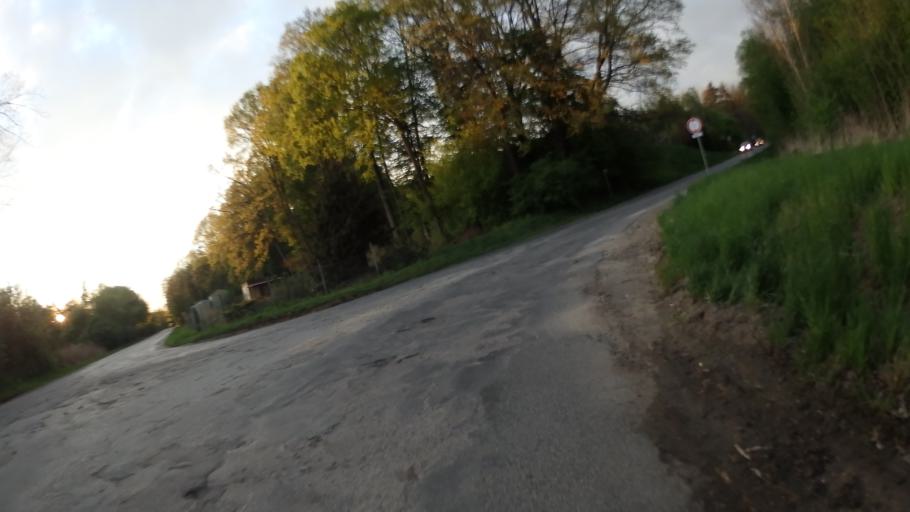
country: CZ
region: South Moravian
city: Strelice
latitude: 49.1498
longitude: 16.4640
